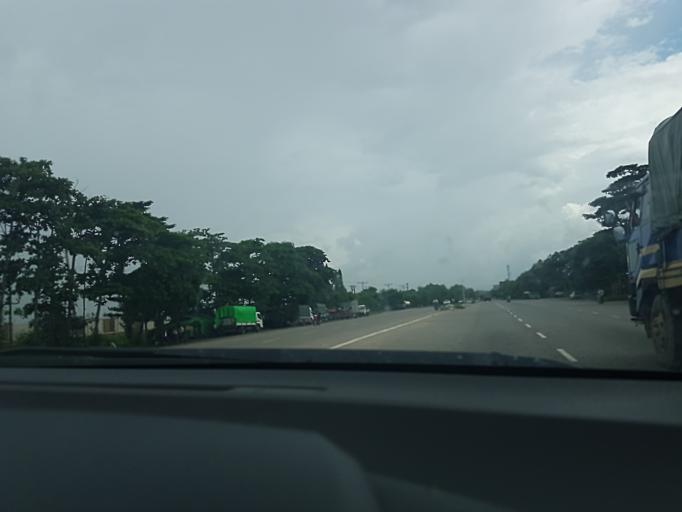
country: MM
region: Bago
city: Thanatpin
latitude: 17.0525
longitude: 96.1475
